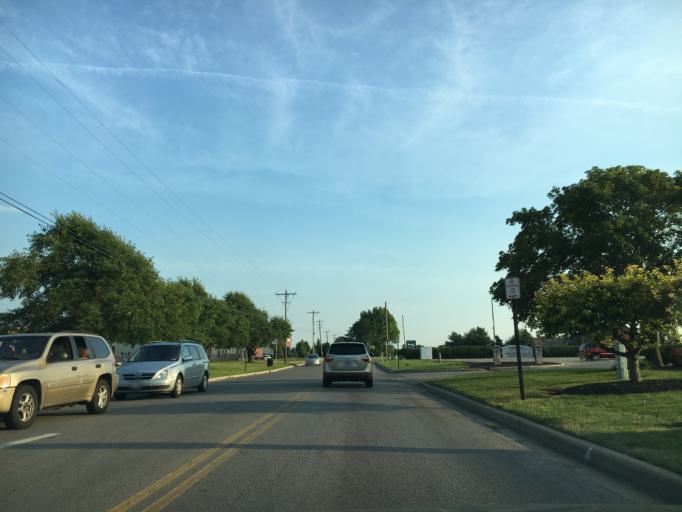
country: US
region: Ohio
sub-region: Franklin County
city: Lincoln Village
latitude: 39.9509
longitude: -83.1468
